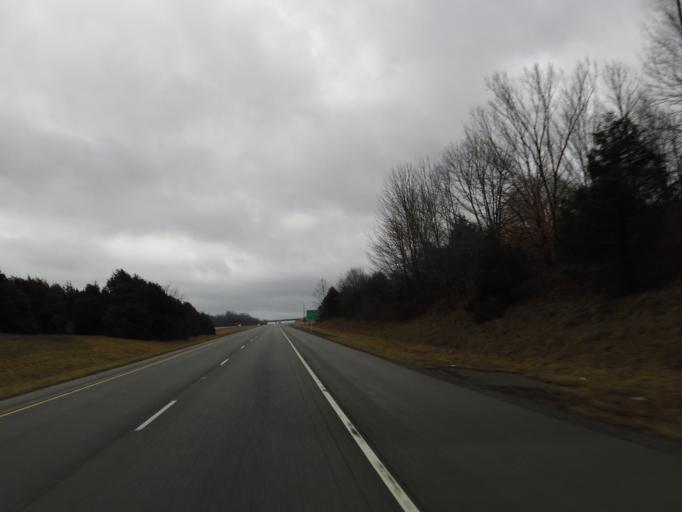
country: US
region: Illinois
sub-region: Johnson County
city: Goreville
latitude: 37.5395
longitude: -88.9291
